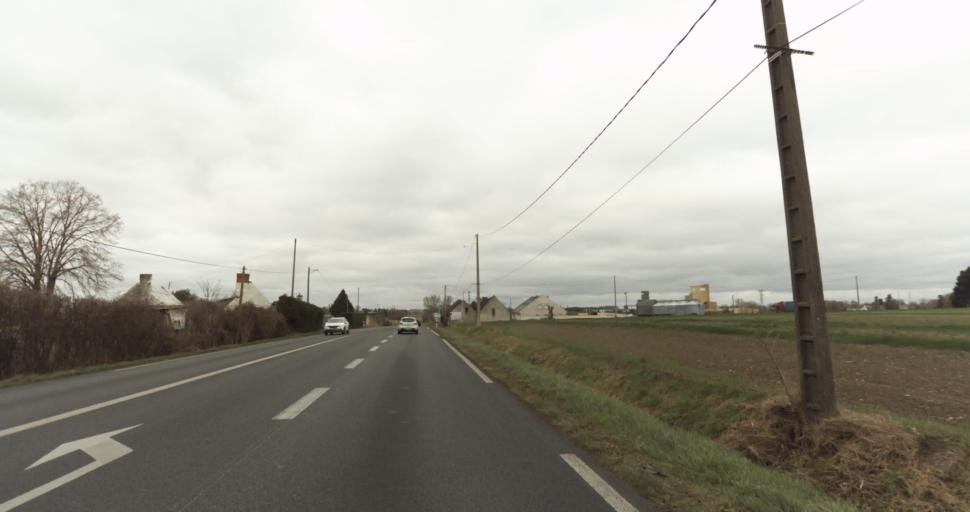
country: FR
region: Pays de la Loire
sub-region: Departement de Maine-et-Loire
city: Vivy
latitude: 47.3610
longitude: -0.0894
